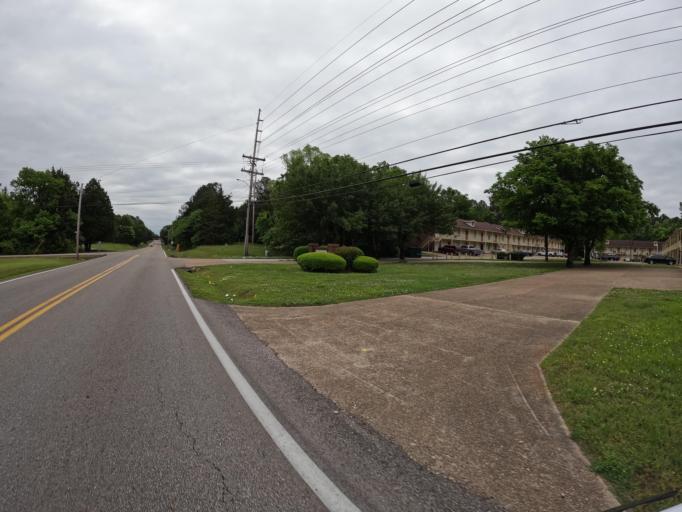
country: US
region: Mississippi
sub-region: Lee County
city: Tupelo
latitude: 34.2647
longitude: -88.7550
